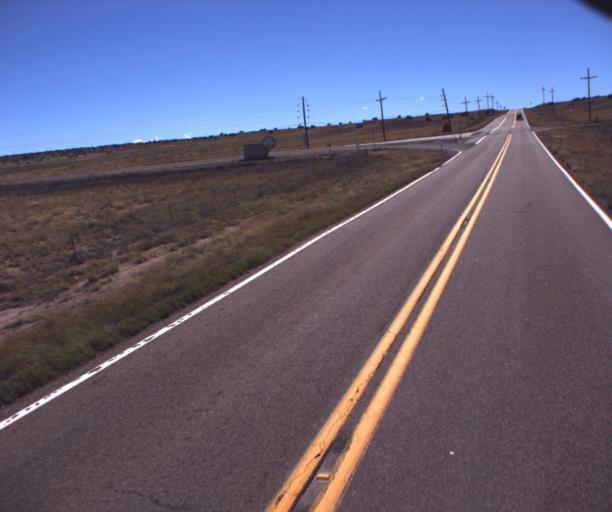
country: US
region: Arizona
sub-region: Apache County
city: Saint Johns
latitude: 34.5716
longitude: -109.3371
